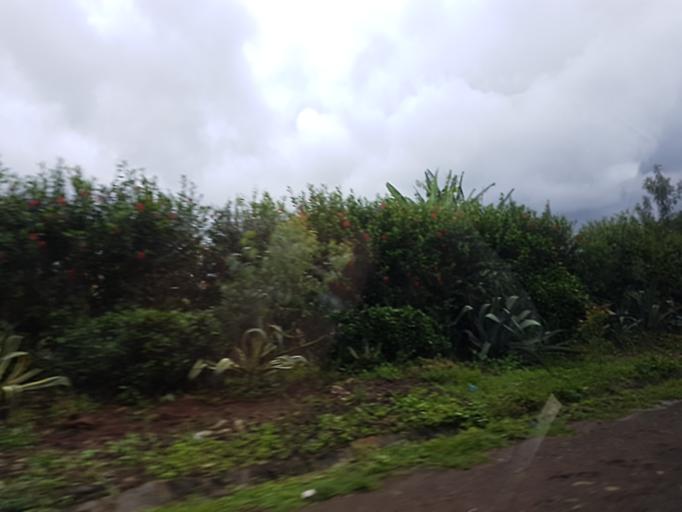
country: KE
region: Kajiado
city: Ngong
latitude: -1.3552
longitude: 36.7362
